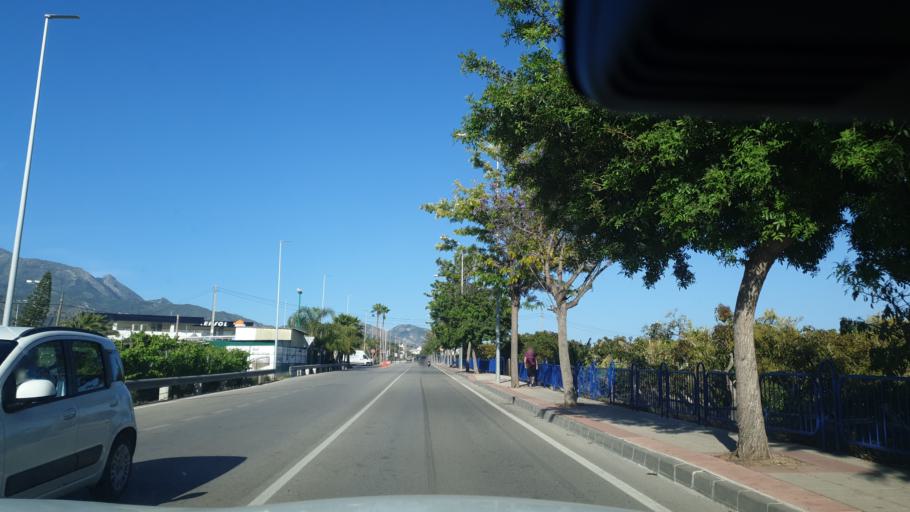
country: ES
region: Andalusia
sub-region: Provincia de Malaga
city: Nerja
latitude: 36.7465
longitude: -3.8924
